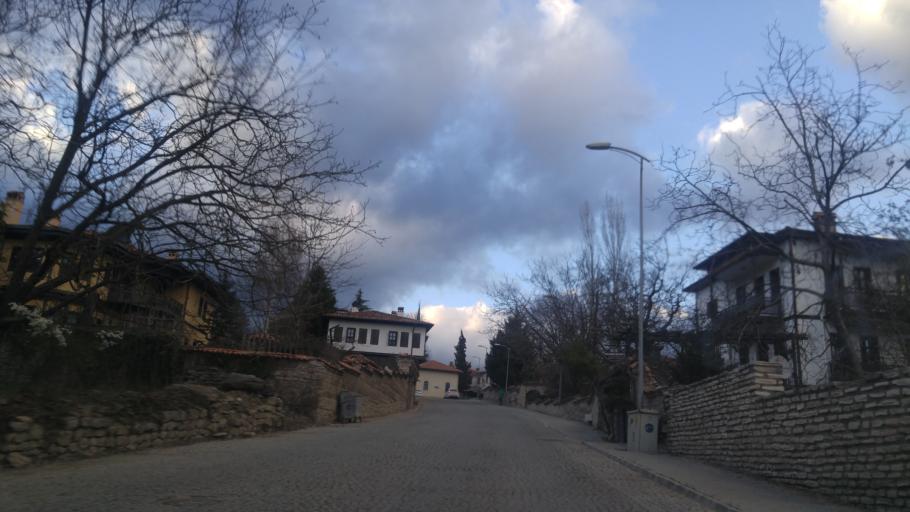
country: TR
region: Karabuk
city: Safranbolu
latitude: 41.2610
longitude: 32.6750
